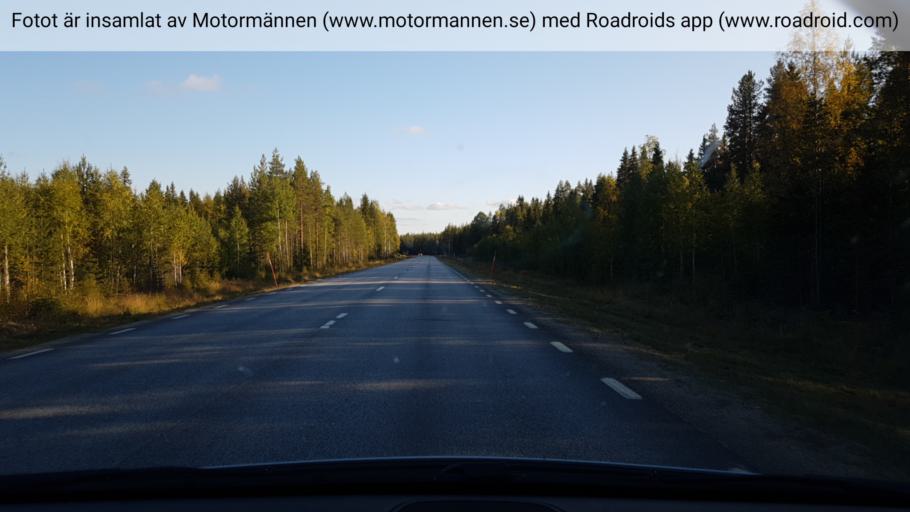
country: SE
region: Vaesterbotten
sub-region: Vannas Kommun
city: Vaennaes
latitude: 63.9526
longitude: 19.7568
